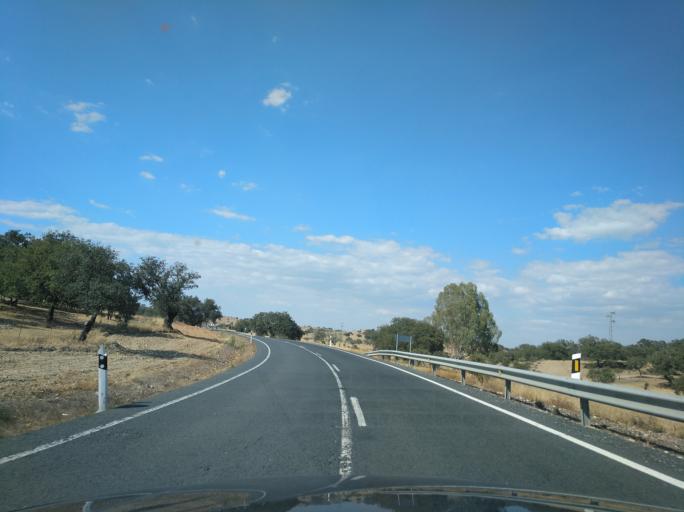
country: ES
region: Andalusia
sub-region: Provincia de Huelva
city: Cabezas Rubias
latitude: 37.6657
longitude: -7.1097
